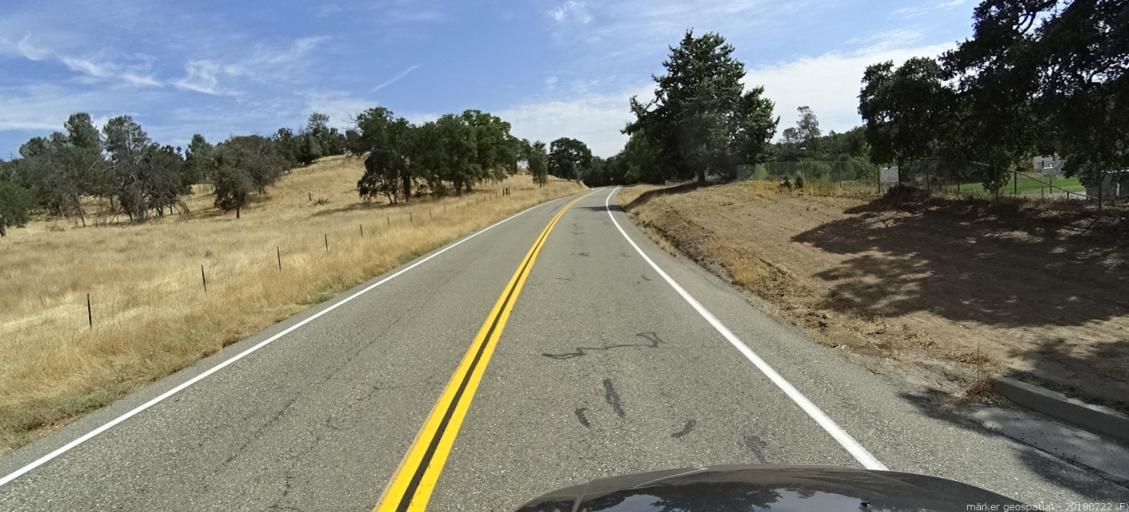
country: US
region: California
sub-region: Madera County
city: Coarsegold
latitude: 37.2566
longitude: -119.7186
